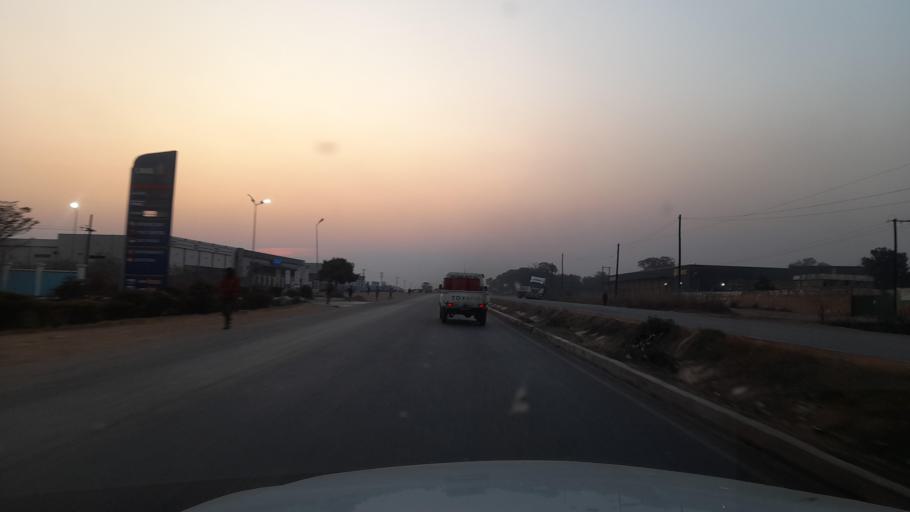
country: ZM
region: Copperbelt
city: Kitwe
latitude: -12.7708
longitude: 28.1835
